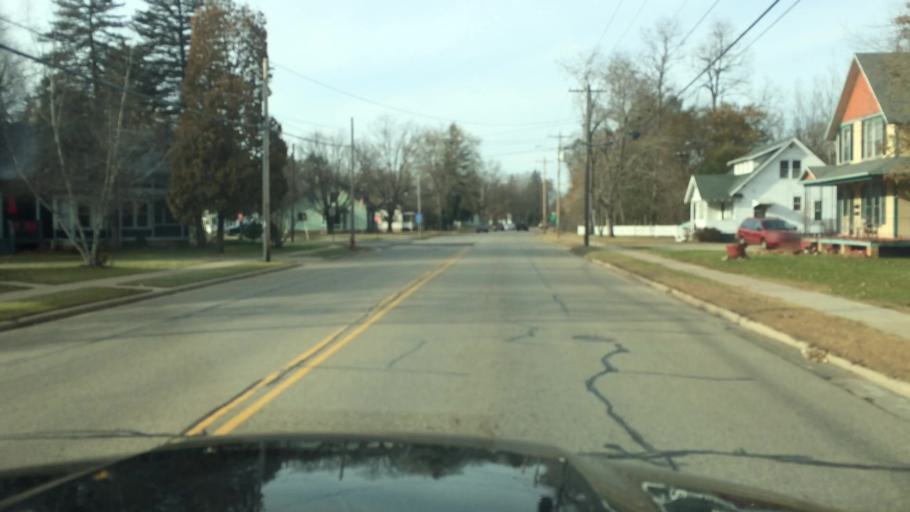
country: US
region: Wisconsin
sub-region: Waupaca County
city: Waupaca
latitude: 44.3523
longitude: -89.0755
